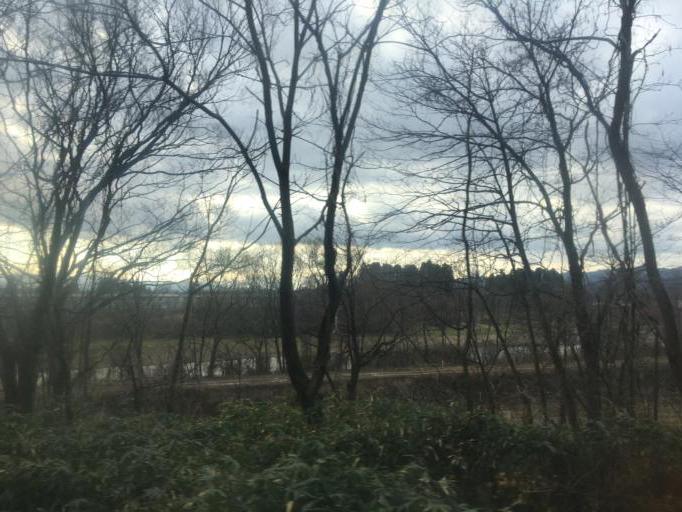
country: JP
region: Akita
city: Odate
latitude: 40.2802
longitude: 140.5218
